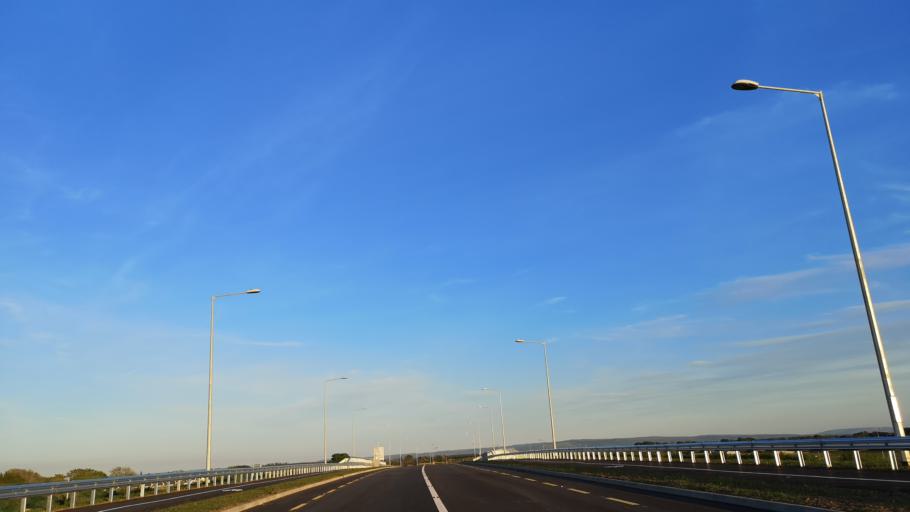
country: IE
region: Connaught
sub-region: County Galway
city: Athenry
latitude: 53.2966
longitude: -8.7617
